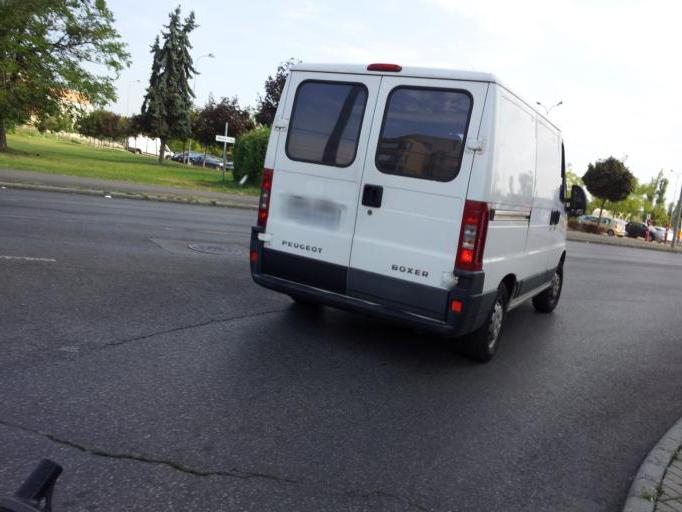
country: HU
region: Budapest
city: Budapest IX. keruelet
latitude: 47.4710
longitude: 19.0826
